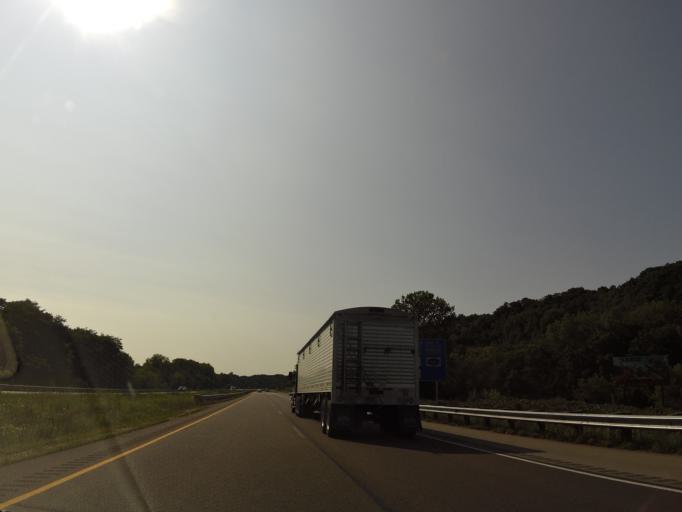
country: US
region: Wisconsin
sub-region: La Crosse County
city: West Salem
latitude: 43.8709
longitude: -91.1395
